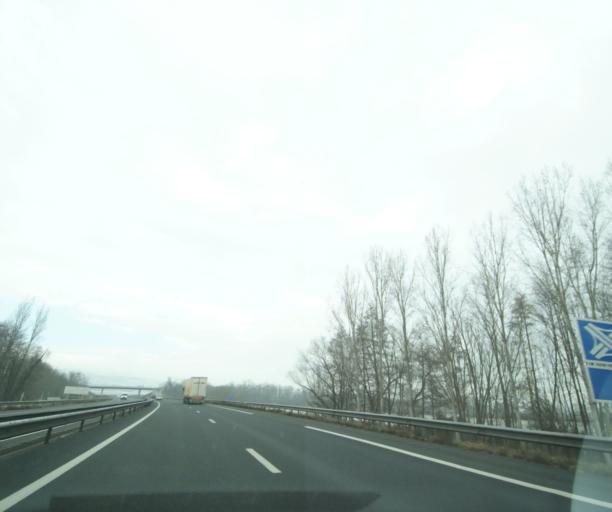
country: FR
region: Auvergne
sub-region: Departement du Puy-de-Dome
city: Saint-Bonnet-pres-Riom
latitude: 45.9475
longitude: 3.1198
